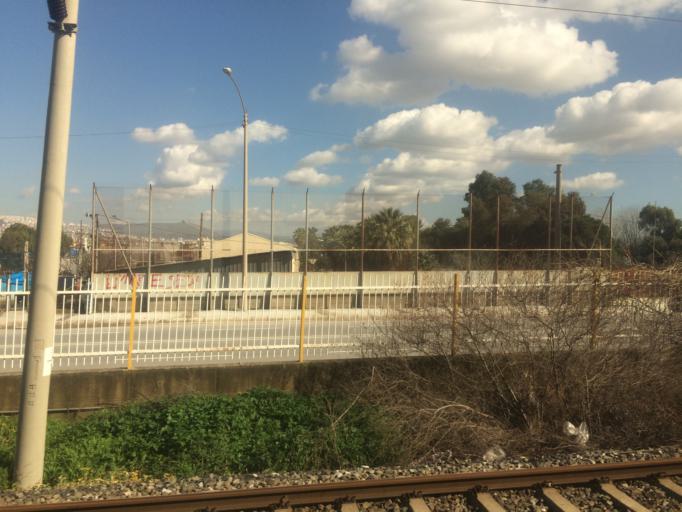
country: TR
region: Izmir
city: Izmir
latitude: 38.4583
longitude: 27.1681
